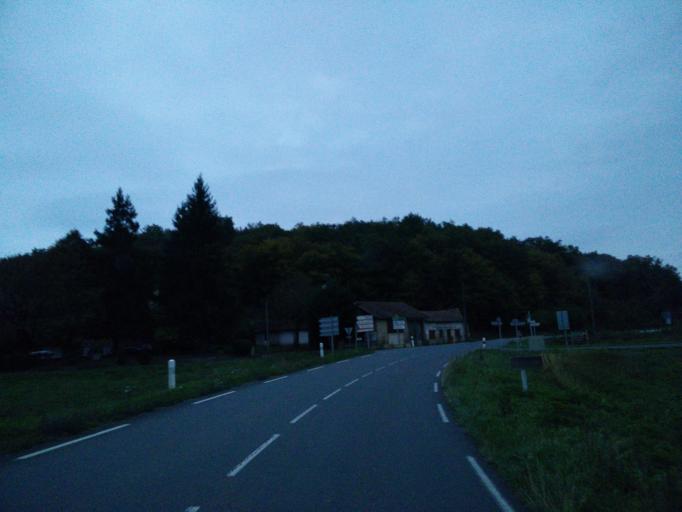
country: FR
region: Aquitaine
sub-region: Departement de la Dordogne
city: Saint-Cyprien
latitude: 44.9175
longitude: 1.1070
